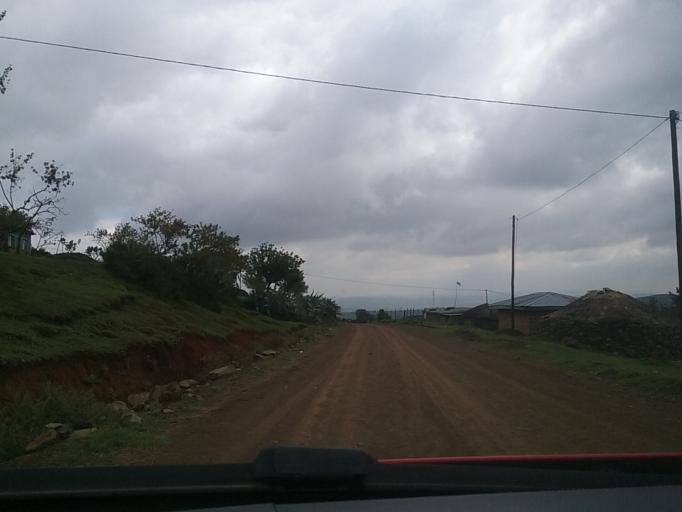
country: LS
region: Berea
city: Teyateyaneng
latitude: -29.2456
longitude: 27.8413
